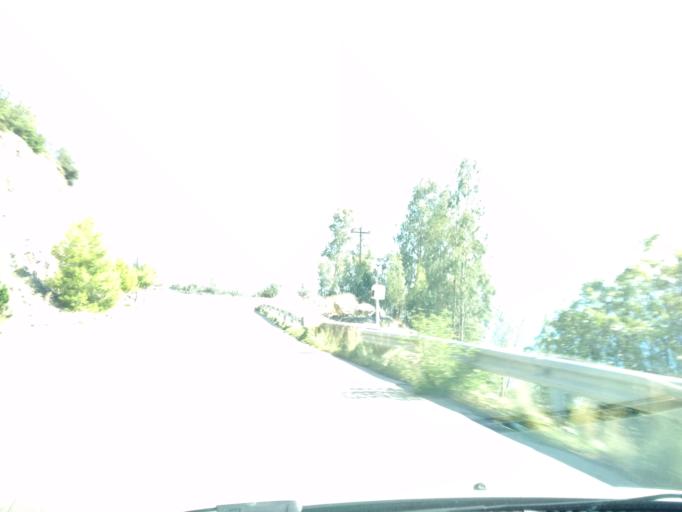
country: GR
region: Central Greece
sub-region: Nomos Evvoias
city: Oreoi
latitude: 38.8453
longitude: 23.0723
